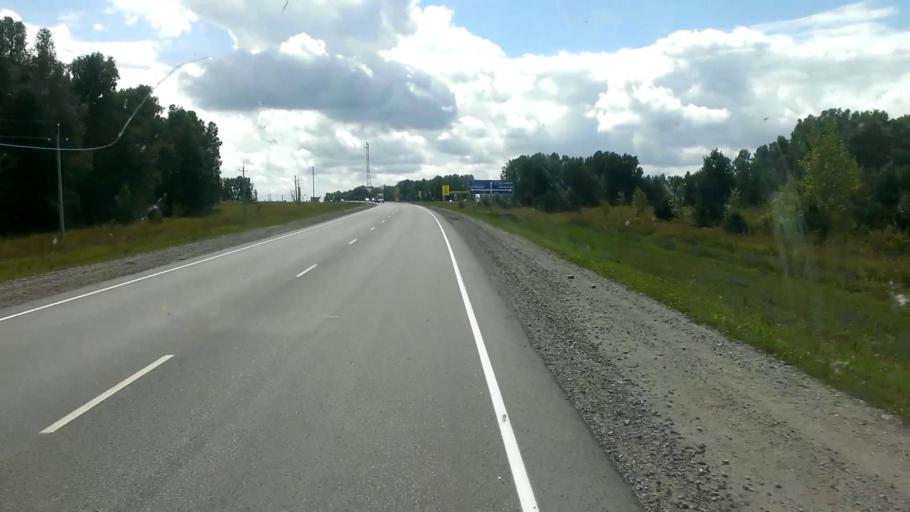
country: RU
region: Altai Krai
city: Troitskoye
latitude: 52.9721
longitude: 84.7480
